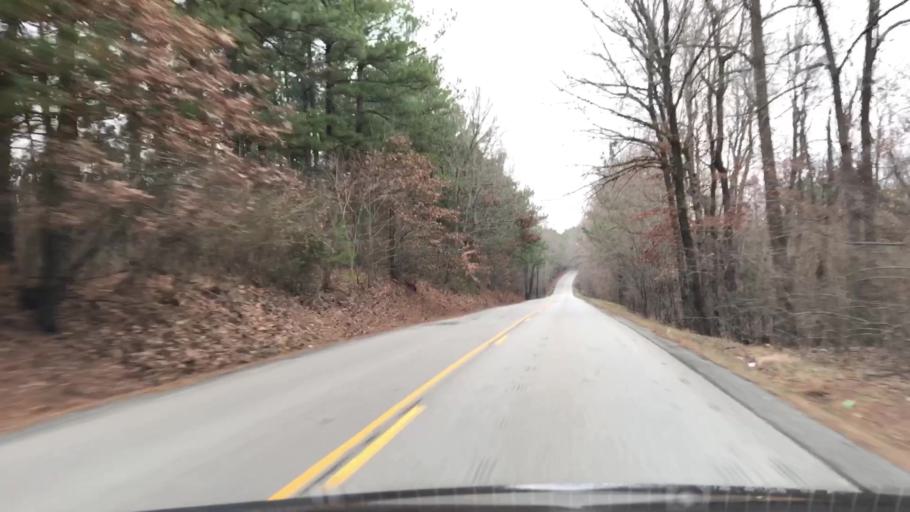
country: US
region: Kentucky
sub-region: Muhlenberg County
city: Morehead
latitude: 37.2832
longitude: -87.2096
